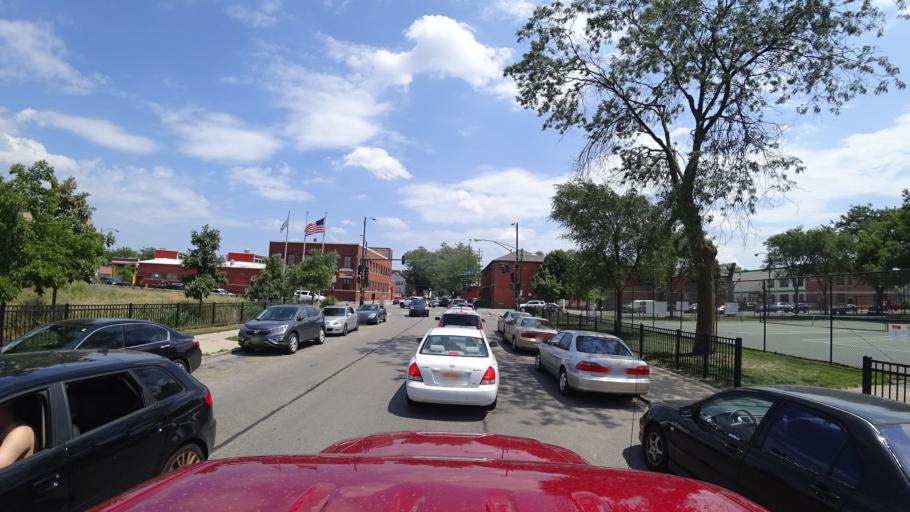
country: US
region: Illinois
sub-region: Cook County
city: Chicago
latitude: 41.8416
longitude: -87.6470
